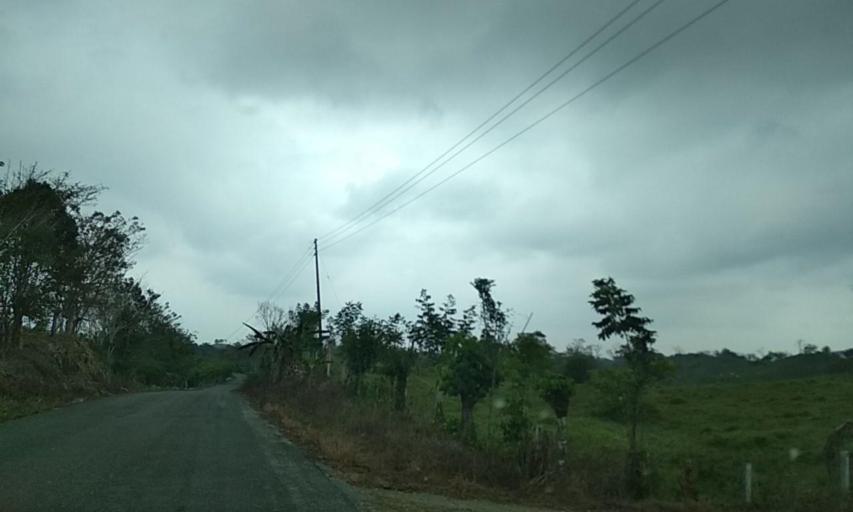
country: MX
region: Tabasco
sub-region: Huimanguillo
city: Francisco Rueda
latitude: 17.5752
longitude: -94.1037
